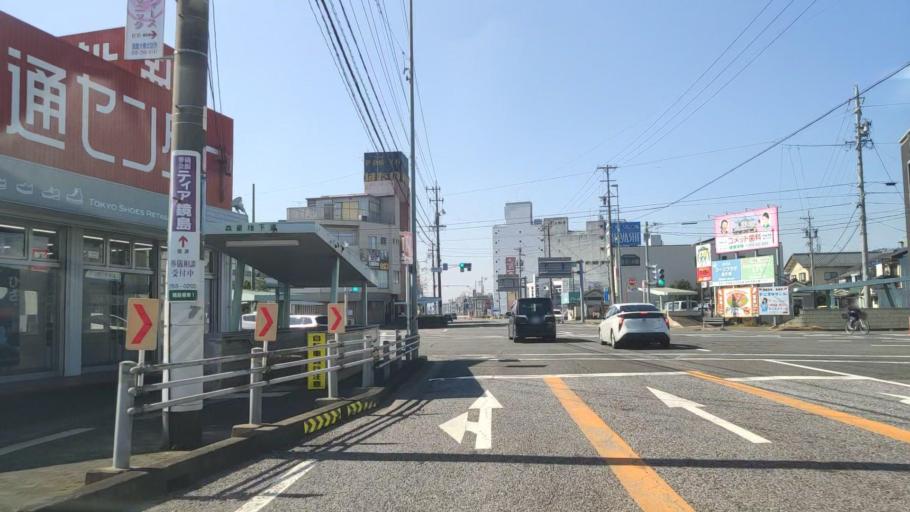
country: JP
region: Gifu
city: Gifu-shi
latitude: 35.4122
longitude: 136.7278
